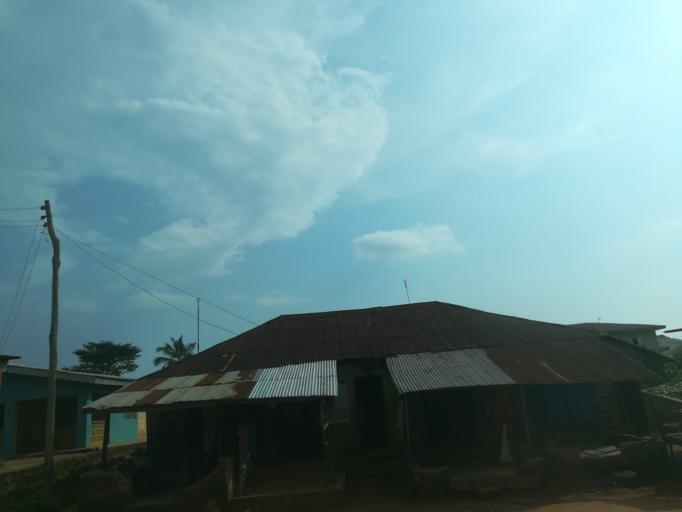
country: NG
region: Lagos
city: Ikorodu
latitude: 6.6656
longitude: 3.6702
